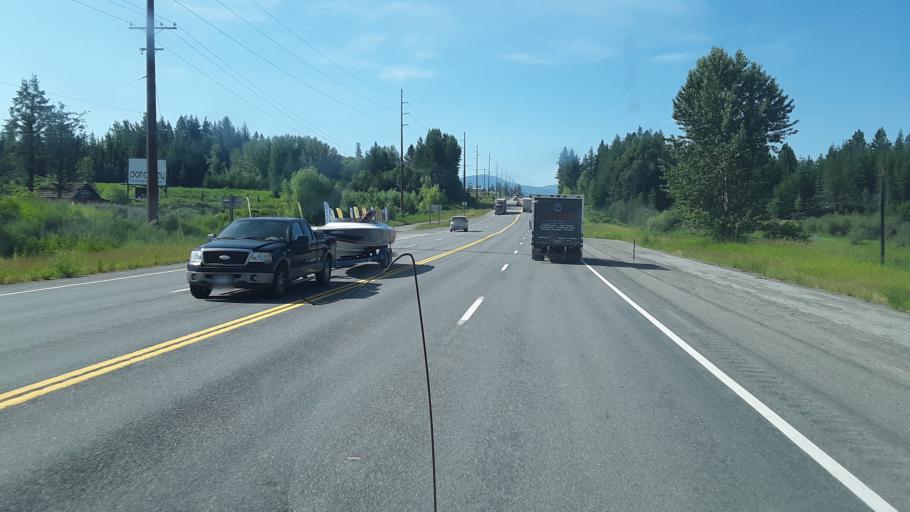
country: US
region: Idaho
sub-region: Bonner County
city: Ponderay
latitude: 48.3190
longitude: -116.5463
